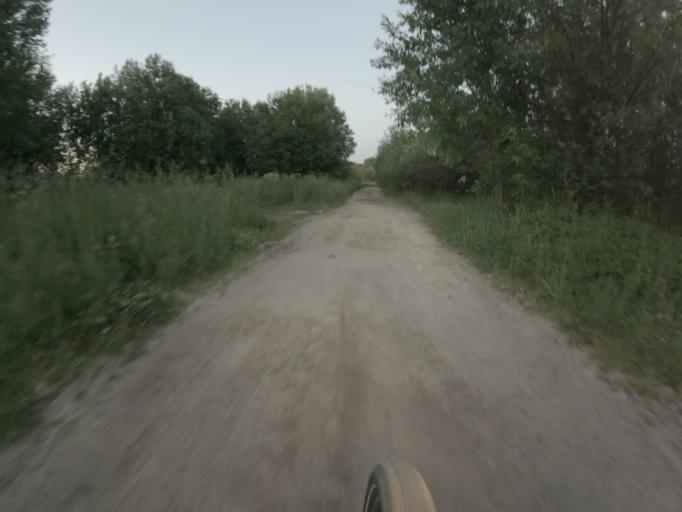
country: RU
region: Leningrad
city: Imeni Sverdlova
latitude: 59.7825
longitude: 30.6821
